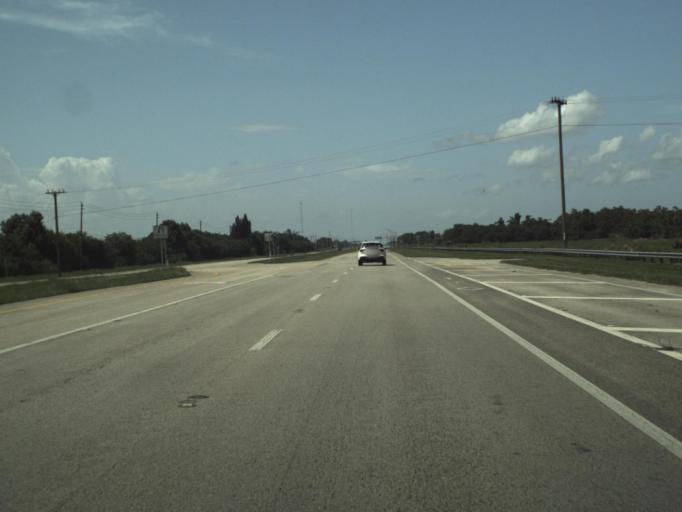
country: US
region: Florida
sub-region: Palm Beach County
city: Villages of Oriole
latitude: 26.5193
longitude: -80.2052
